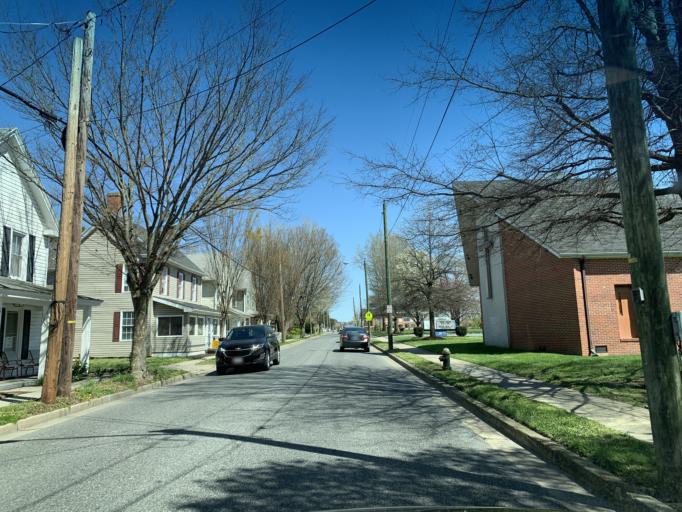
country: US
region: Maryland
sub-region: Talbot County
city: Easton
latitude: 38.7762
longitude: -76.0656
